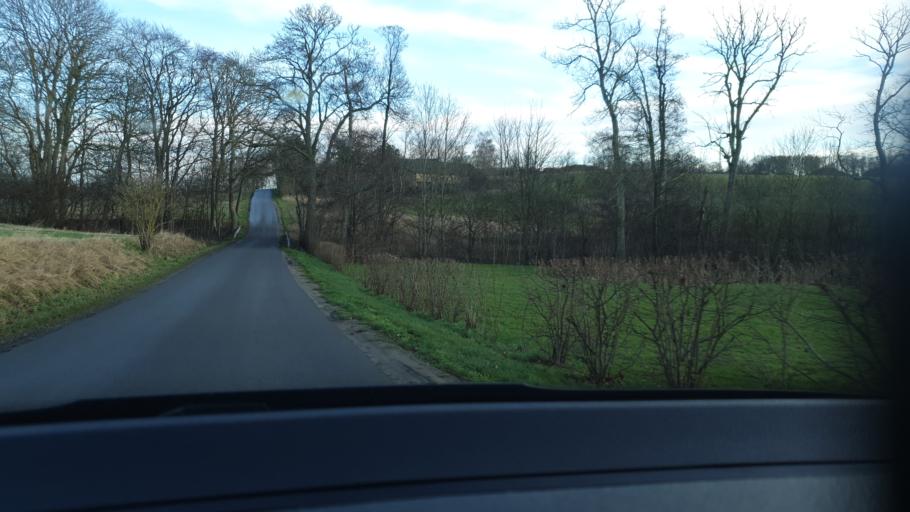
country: DK
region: Zealand
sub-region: Odsherred Kommune
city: Hojby
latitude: 55.9189
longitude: 11.6265
